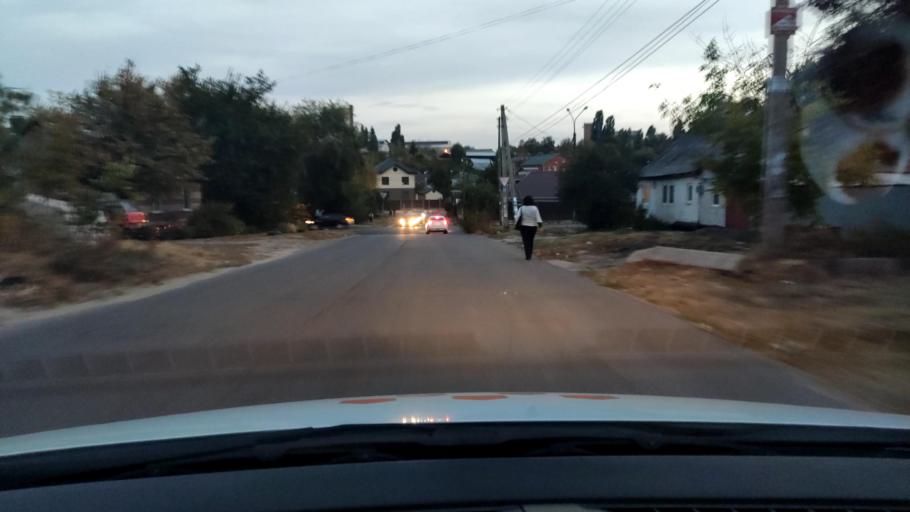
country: RU
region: Voronezj
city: Voronezh
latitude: 51.6953
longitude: 39.1691
